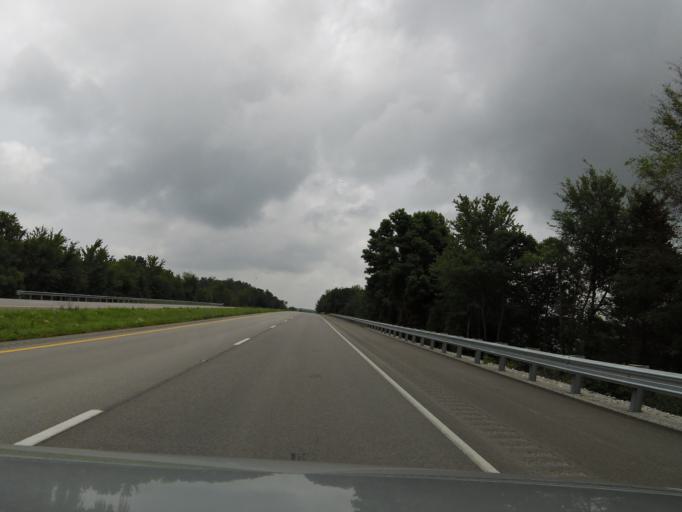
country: US
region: Kentucky
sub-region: Grayson County
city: Leitchfield
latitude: 37.4454
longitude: -86.3487
